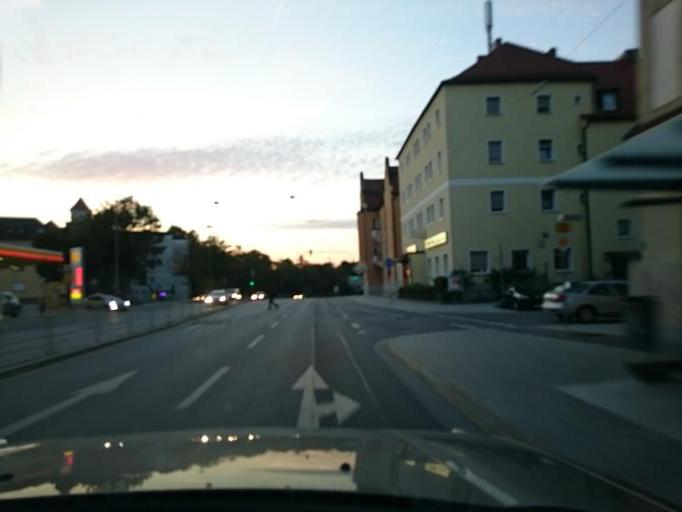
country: DE
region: Bavaria
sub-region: Upper Palatinate
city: Regensburg
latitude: 49.0101
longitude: 12.1121
